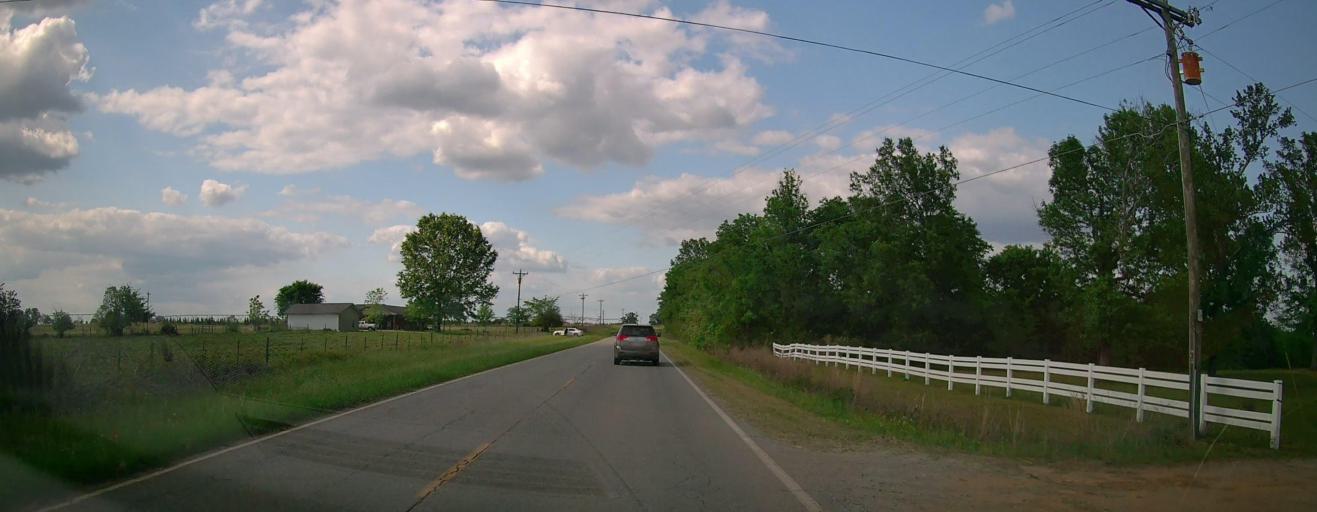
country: US
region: Georgia
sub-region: Laurens County
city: East Dublin
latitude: 32.6034
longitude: -82.8671
